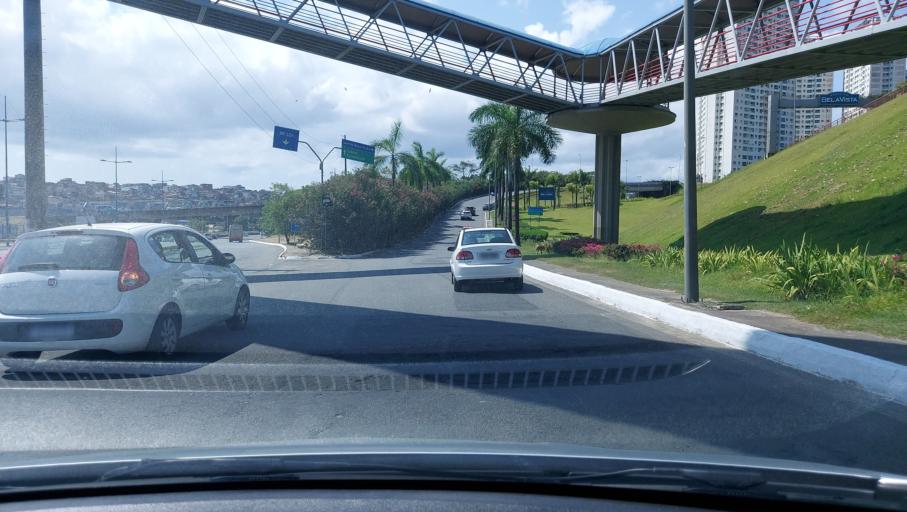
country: BR
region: Bahia
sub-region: Salvador
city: Salvador
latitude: -12.9696
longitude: -38.4756
